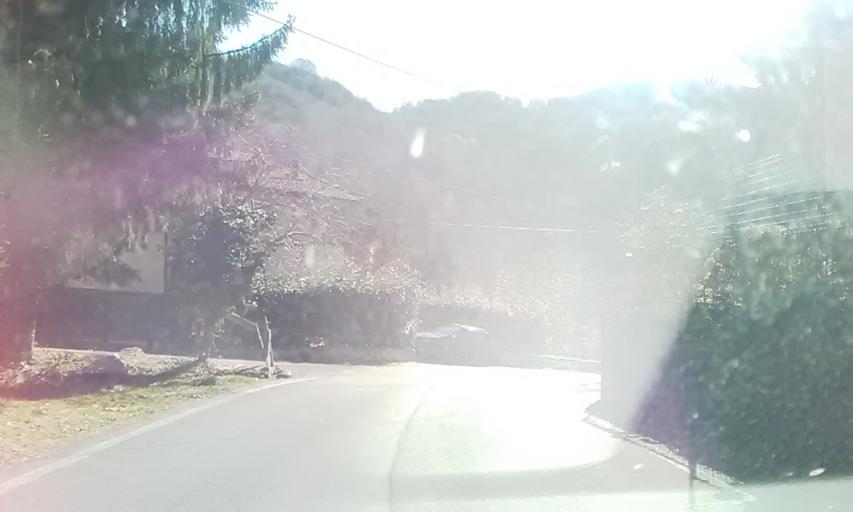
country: IT
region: Piedmont
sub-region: Provincia di Vercelli
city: Breia
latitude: 45.7782
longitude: 8.2876
